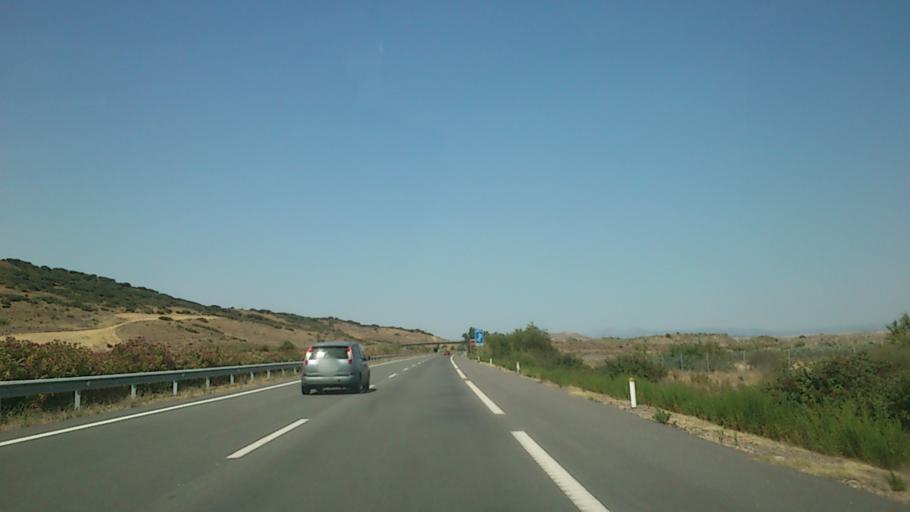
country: ES
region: La Rioja
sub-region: Provincia de La Rioja
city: Pradejon
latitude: 42.3514
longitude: -2.0539
